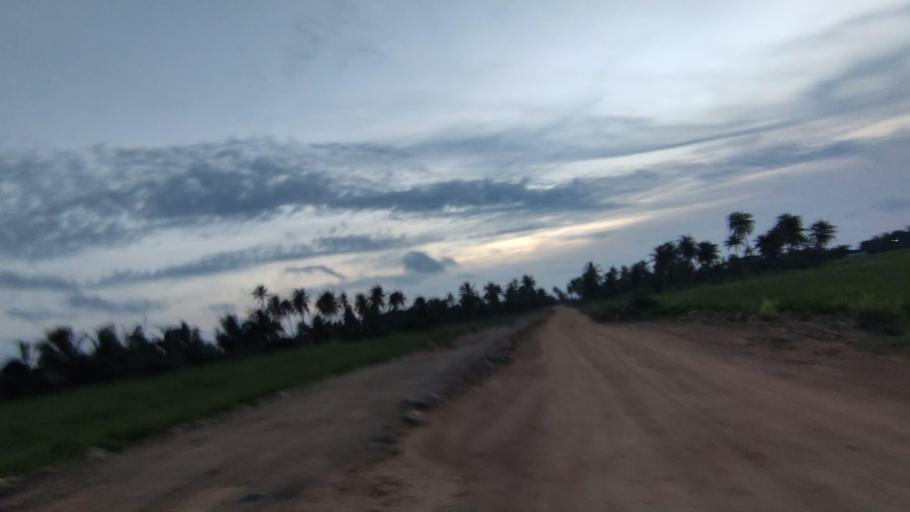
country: IN
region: Kerala
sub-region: Kottayam
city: Kottayam
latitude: 9.6445
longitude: 76.4552
